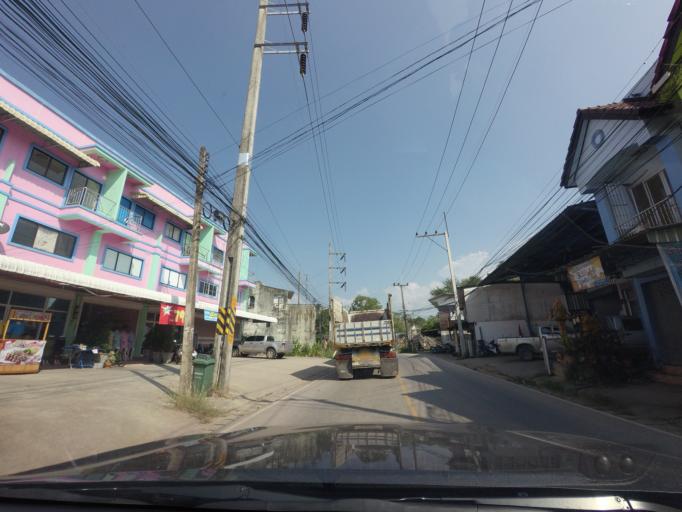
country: TH
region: Phitsanulok
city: Nakhon Thai
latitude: 17.1061
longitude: 100.8412
